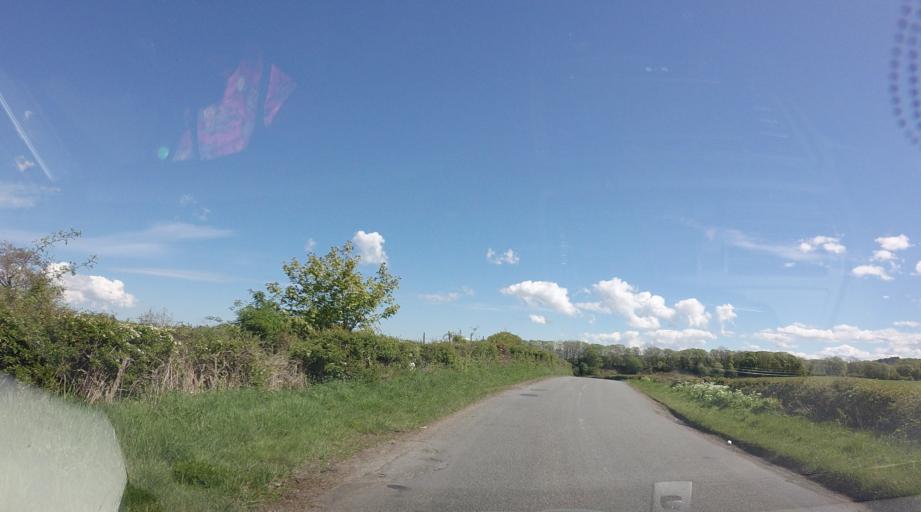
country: GB
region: Scotland
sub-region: Falkirk
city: Polmont
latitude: 55.9727
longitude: -3.6701
